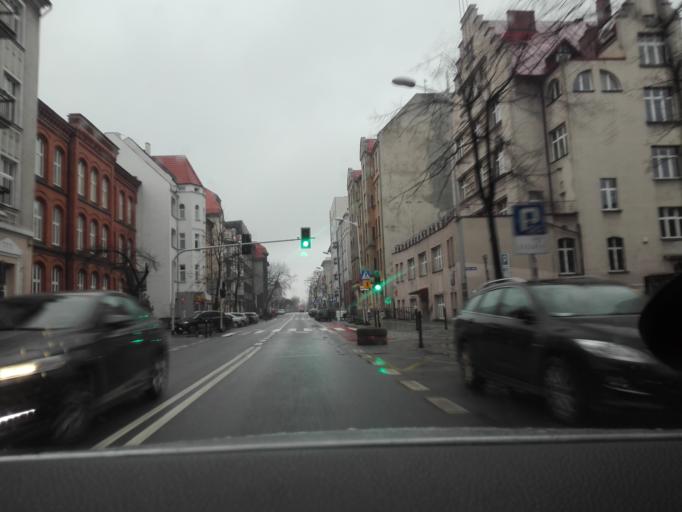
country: PL
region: Silesian Voivodeship
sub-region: Katowice
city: Katowice
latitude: 50.2543
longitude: 19.0213
